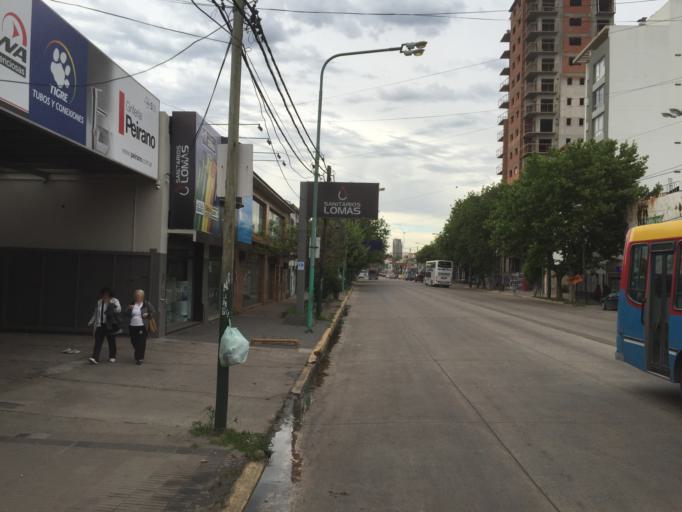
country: AR
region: Buenos Aires
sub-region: Partido de Lomas de Zamora
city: Lomas de Zamora
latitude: -34.7509
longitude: -58.3945
